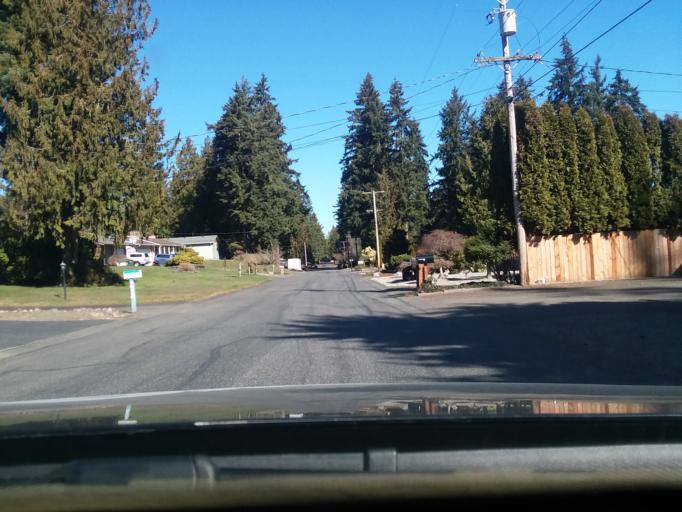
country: US
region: Washington
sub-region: Pierce County
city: Summit
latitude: 47.1626
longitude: -122.3435
